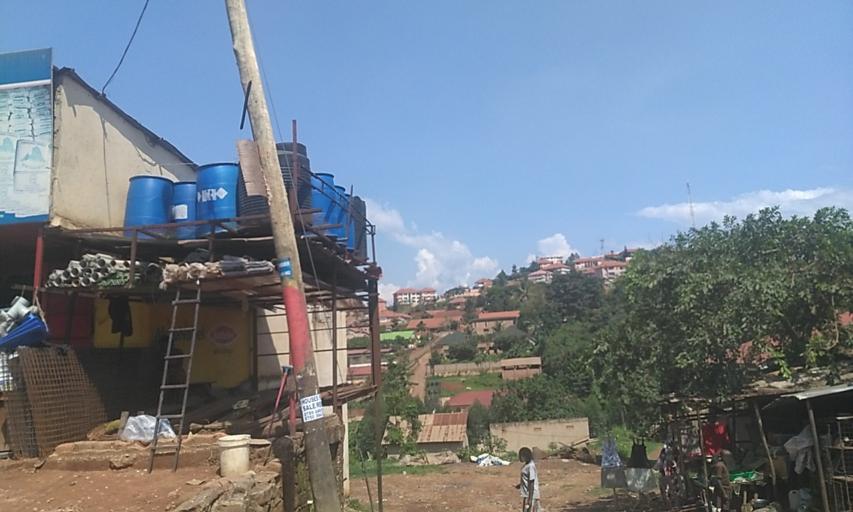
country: UG
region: Central Region
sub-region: Wakiso District
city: Kireka
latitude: 0.3711
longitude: 32.6021
